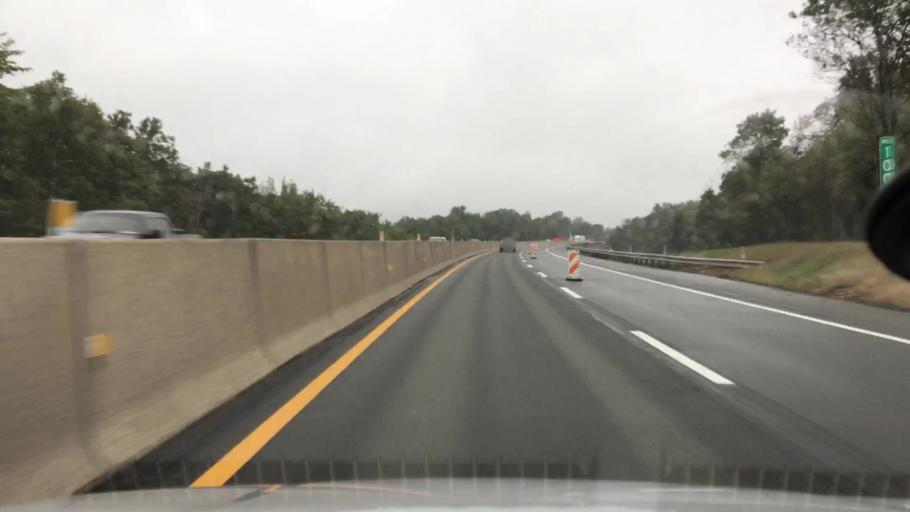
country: US
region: Pennsylvania
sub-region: Luzerne County
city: White Haven
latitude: 41.1304
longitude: -75.7771
